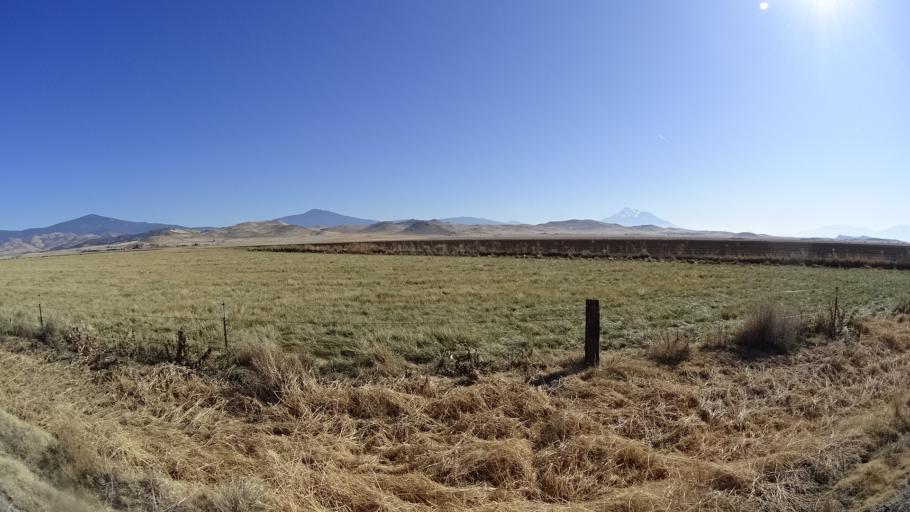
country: US
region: California
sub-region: Siskiyou County
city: Montague
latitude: 41.7903
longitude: -122.4595
